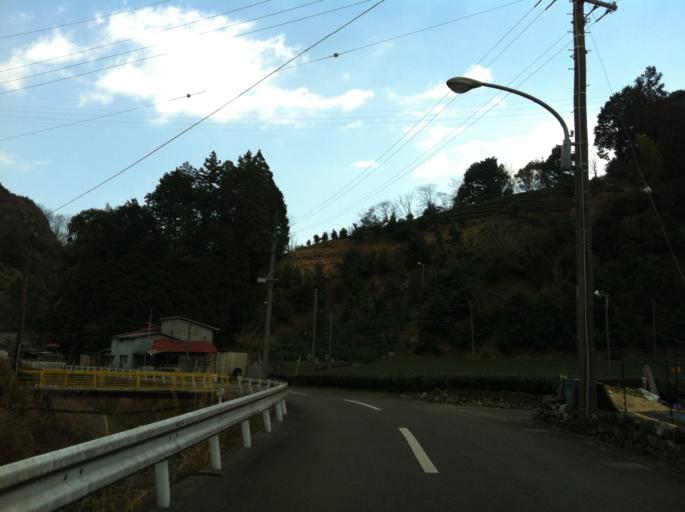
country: JP
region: Shizuoka
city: Shizuoka-shi
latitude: 35.0315
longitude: 138.3351
